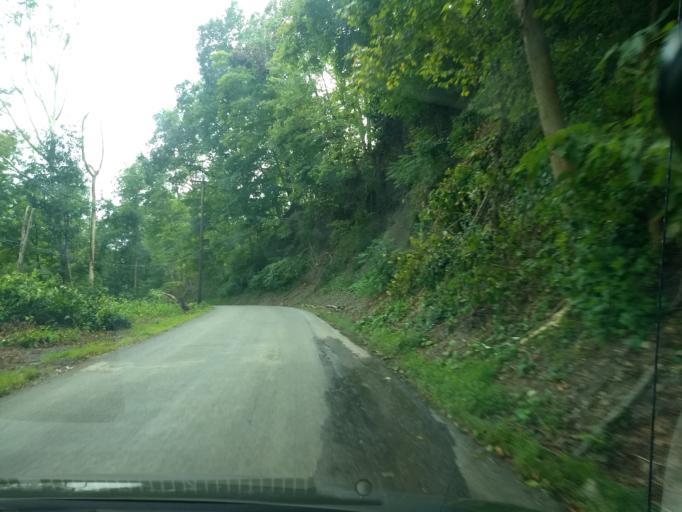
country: US
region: Pennsylvania
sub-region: Westmoreland County
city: Murrysville
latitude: 40.4251
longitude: -79.7256
